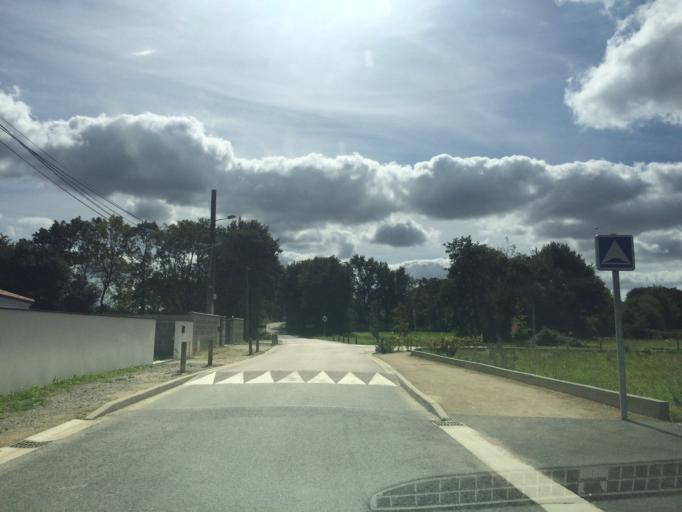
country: FR
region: Pays de la Loire
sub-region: Departement de la Loire-Atlantique
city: Chemere
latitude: 47.1132
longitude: -1.9170
